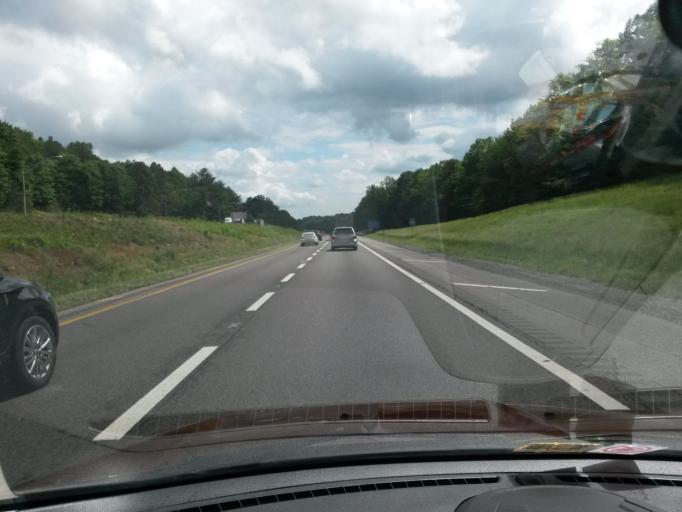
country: US
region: Virginia
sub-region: Carroll County
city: Cana
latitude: 36.5695
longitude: -80.7443
